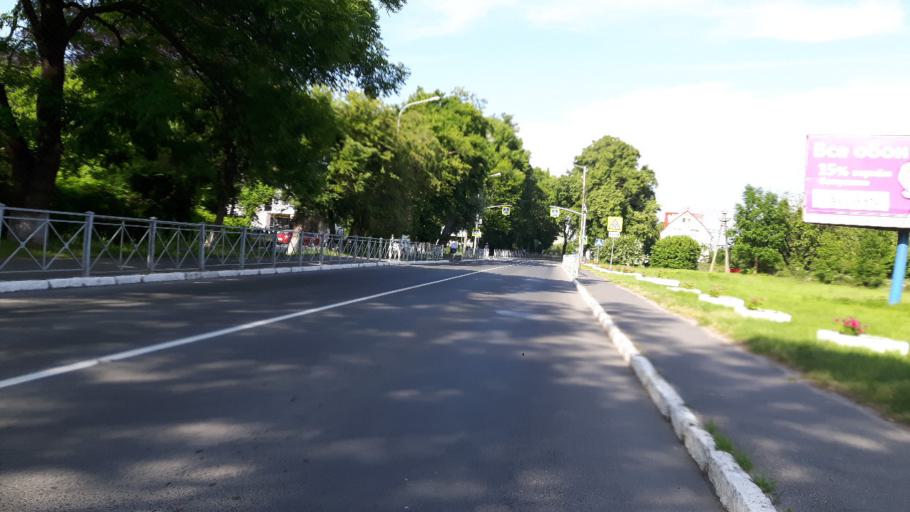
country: RU
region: Kaliningrad
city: Mamonovo
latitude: 54.4614
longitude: 19.9455
